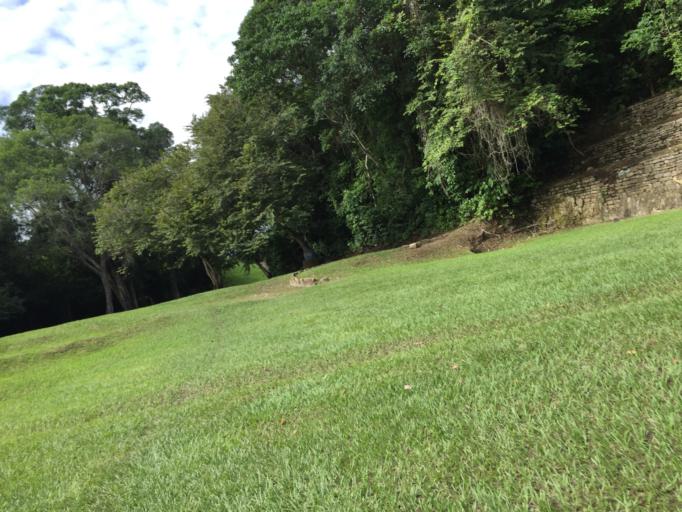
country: MX
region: Veracruz
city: Papantla de Olarte
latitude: 20.4489
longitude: -97.3756
